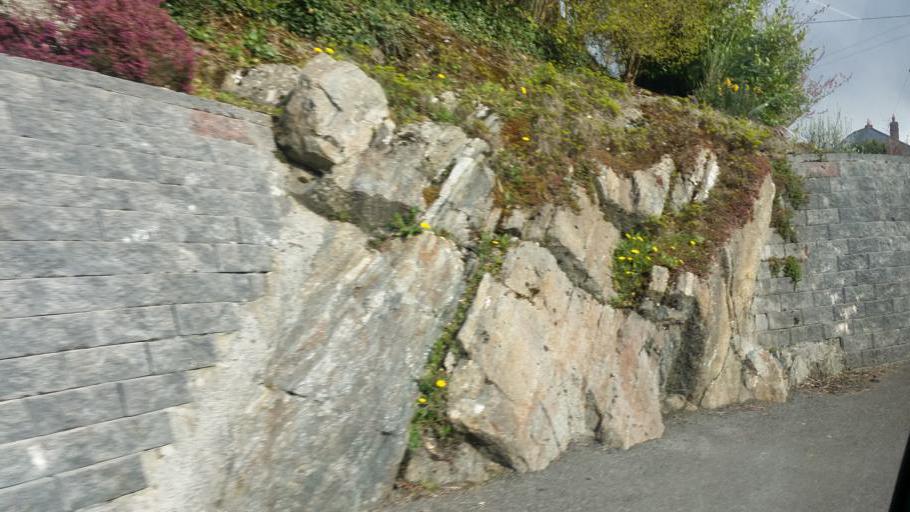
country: IE
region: Connaught
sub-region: County Leitrim
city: Manorhamilton
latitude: 54.3074
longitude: -8.1839
